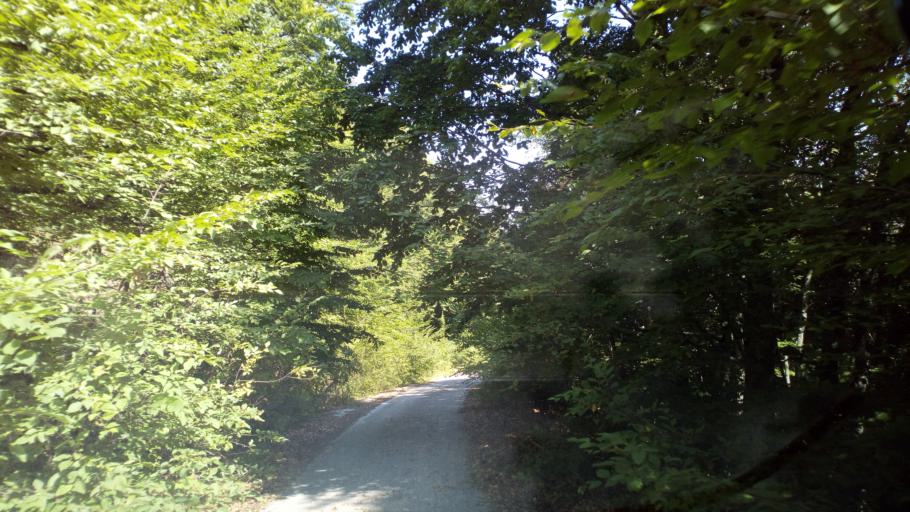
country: GR
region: Central Macedonia
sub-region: Nomos Thessalonikis
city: Sochos
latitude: 40.8267
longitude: 23.3568
